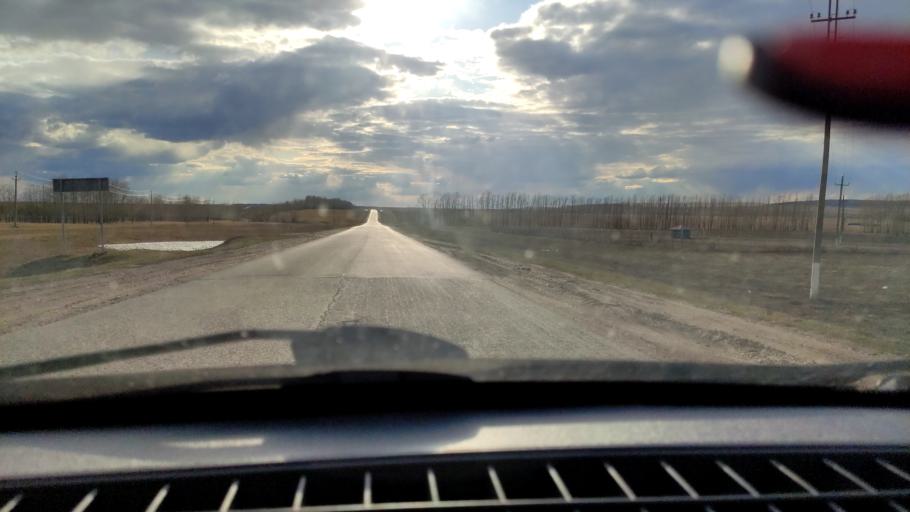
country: RU
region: Bashkortostan
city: Karmaskaly
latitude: 54.3482
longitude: 56.0529
